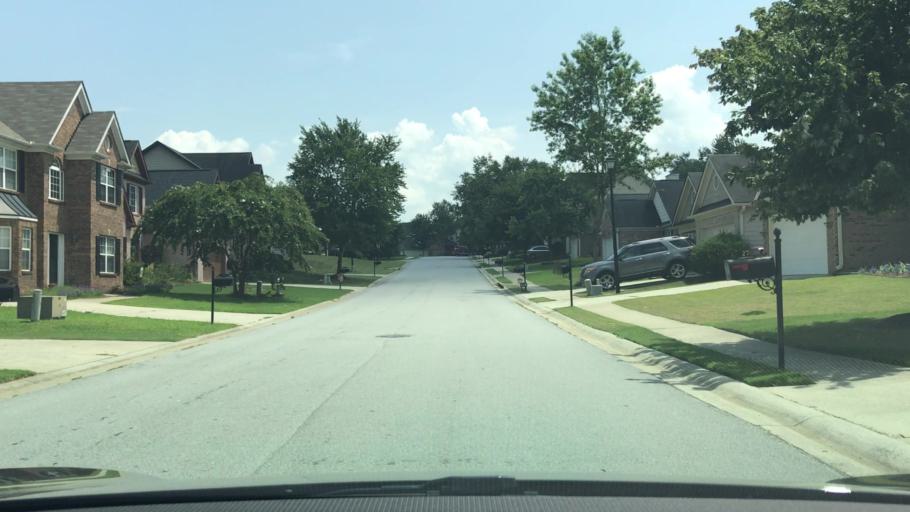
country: US
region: Georgia
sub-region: Jackson County
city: Braselton
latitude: 34.1234
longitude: -83.8248
